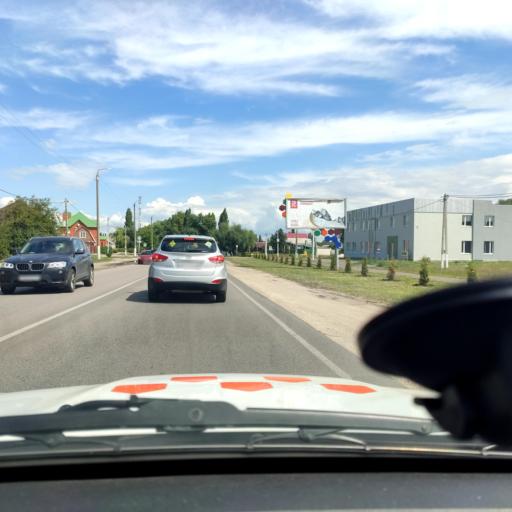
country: RU
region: Voronezj
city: Novaya Usman'
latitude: 51.6321
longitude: 39.4030
